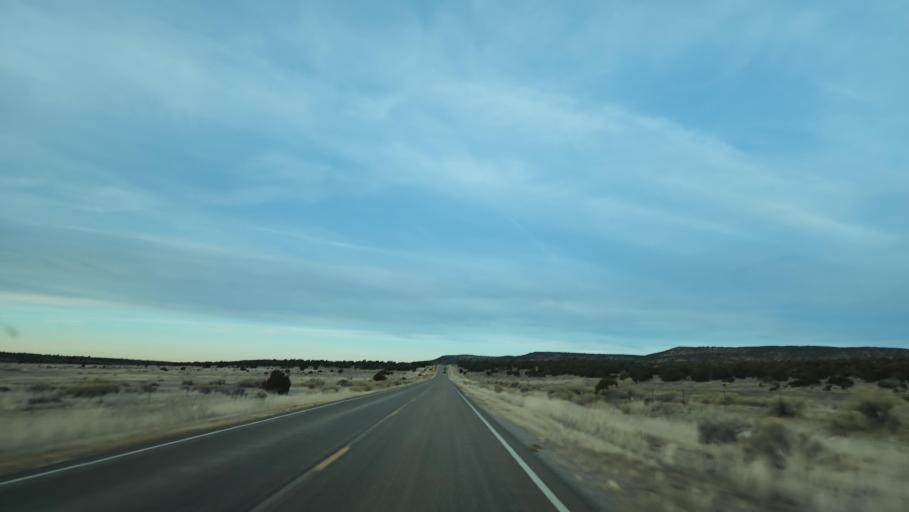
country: US
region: New Mexico
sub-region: Cibola County
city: Grants
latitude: 34.7167
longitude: -107.9837
